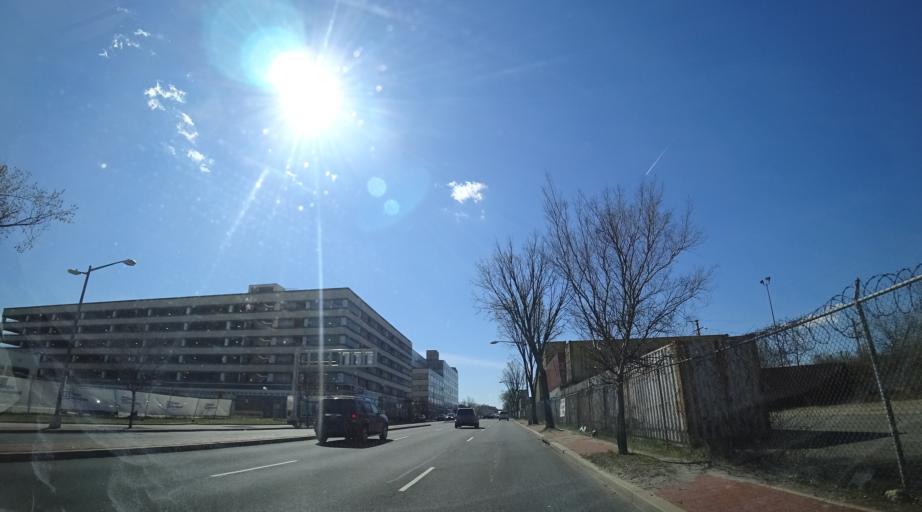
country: US
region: Maryland
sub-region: Prince George's County
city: Mount Rainier
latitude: 38.9167
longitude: -76.9824
